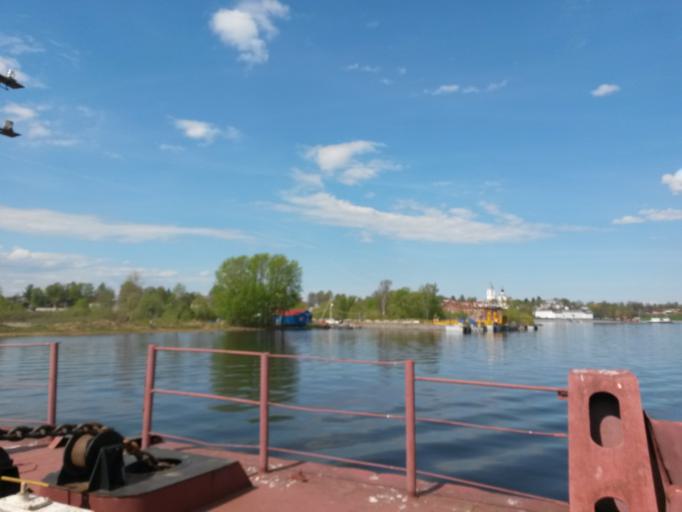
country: RU
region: Jaroslavl
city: Myshkin
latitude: 57.7793
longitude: 38.4544
